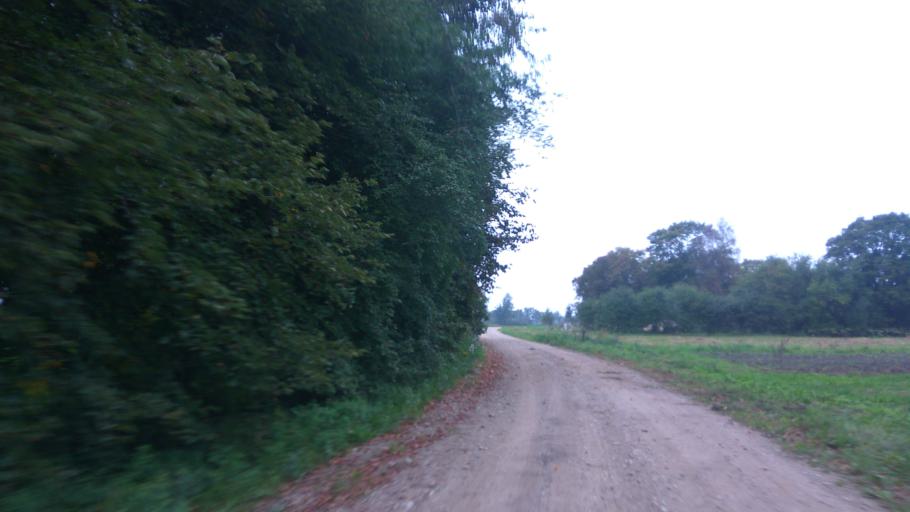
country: LV
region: Rucavas
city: Rucava
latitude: 56.1629
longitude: 21.1750
